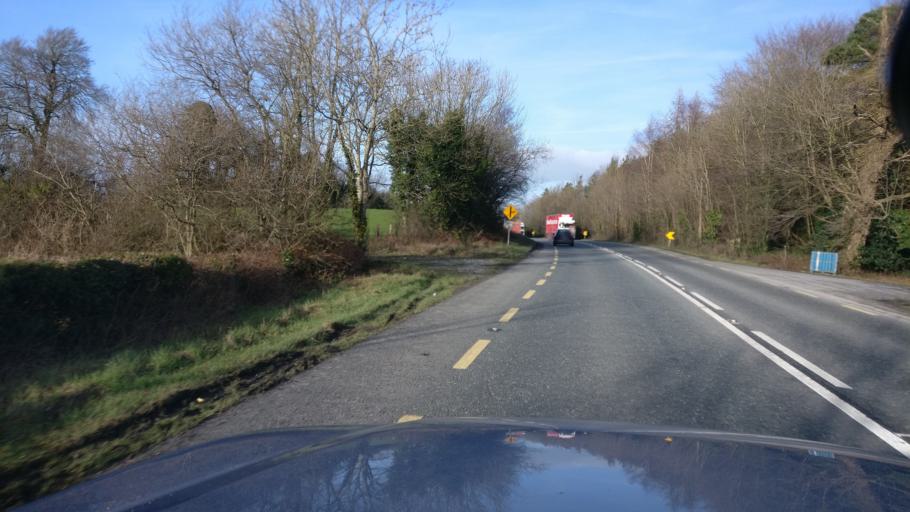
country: IE
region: Leinster
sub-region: Uibh Fhaili
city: Tullamore
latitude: 53.2286
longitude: -7.4757
